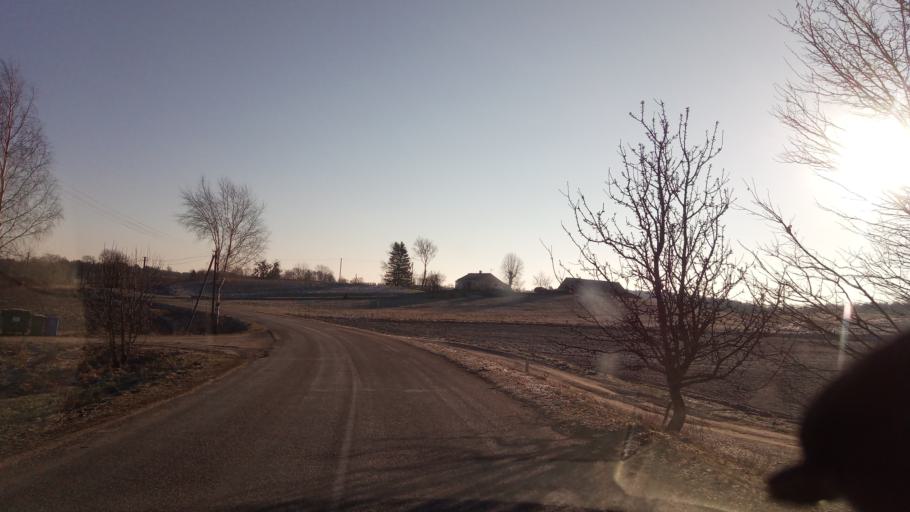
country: LT
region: Alytaus apskritis
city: Druskininkai
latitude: 54.1138
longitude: 24.0123
